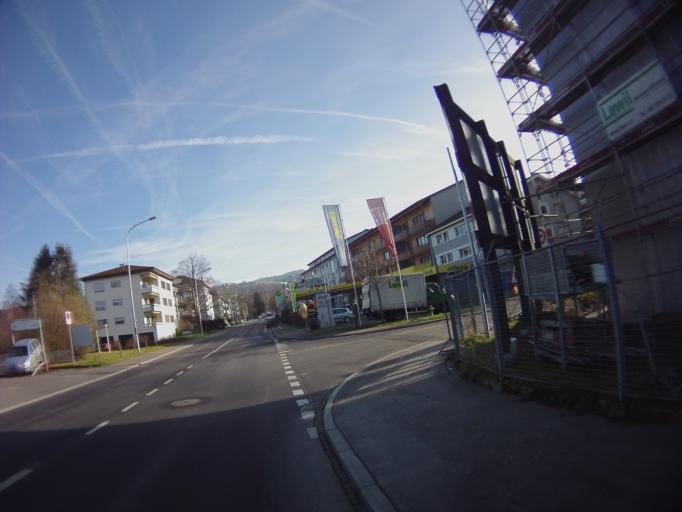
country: CH
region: Zug
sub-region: Zug
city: Zug
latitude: 47.1831
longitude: 8.5235
